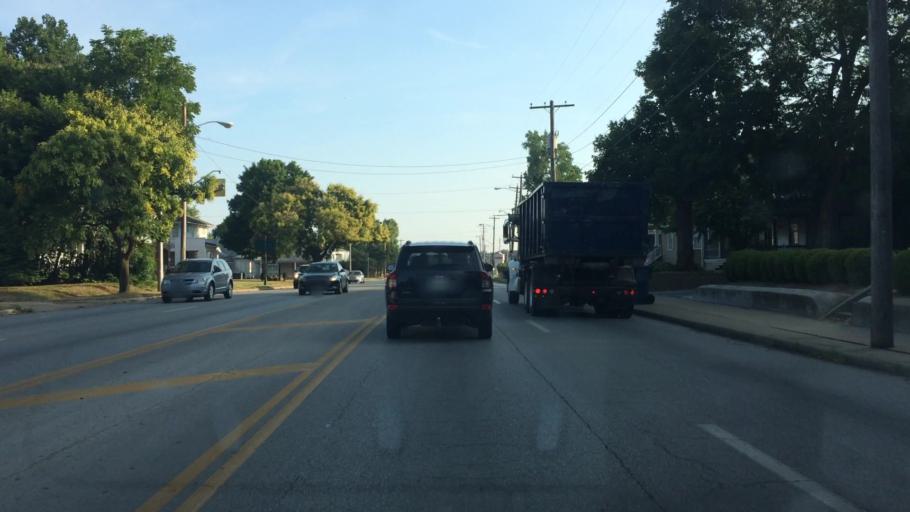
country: US
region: Missouri
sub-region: Greene County
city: Springfield
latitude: 37.2069
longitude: -93.2760
